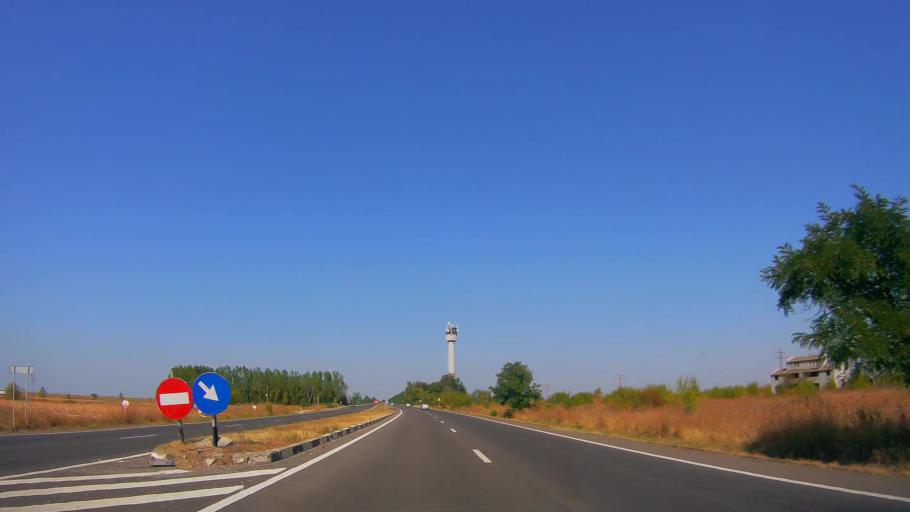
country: RO
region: Giurgiu
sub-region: Comuna Adunatii-Copaceni
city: Adunatii-Copaceni
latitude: 44.2224
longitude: 26.0269
